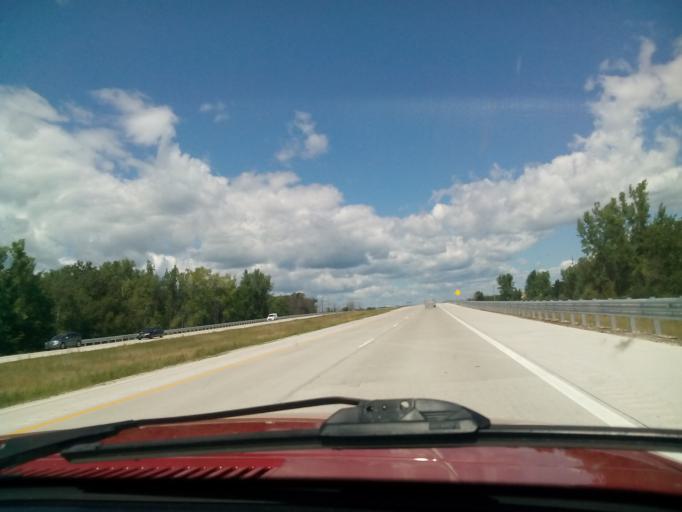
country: US
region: Michigan
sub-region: Bay County
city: Pinconning
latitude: 43.8938
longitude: -84.0198
